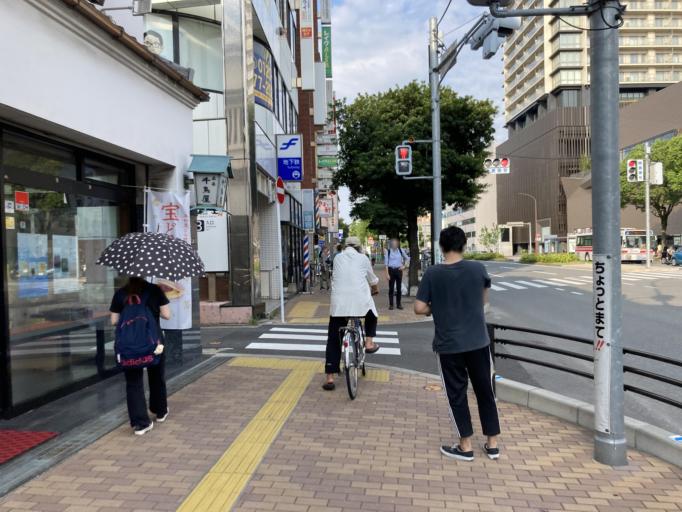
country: JP
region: Fukuoka
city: Fukuoka-shi
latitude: 33.5836
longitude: 130.3590
